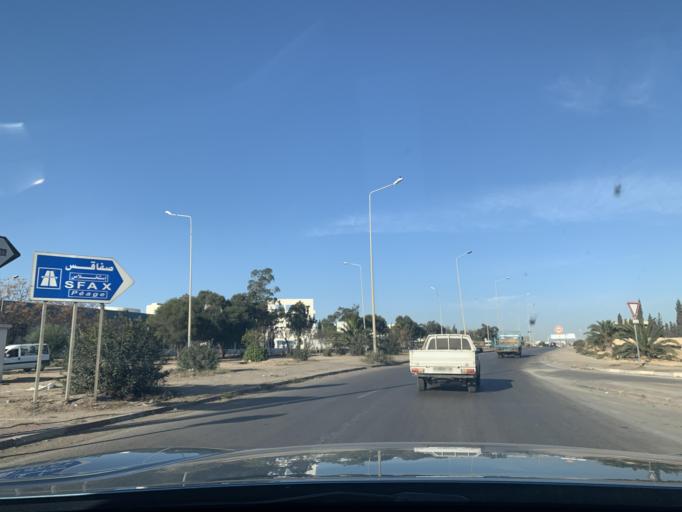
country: DZ
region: Souk Ahras
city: Souk Ahras
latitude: 36.3638
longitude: 8.0062
